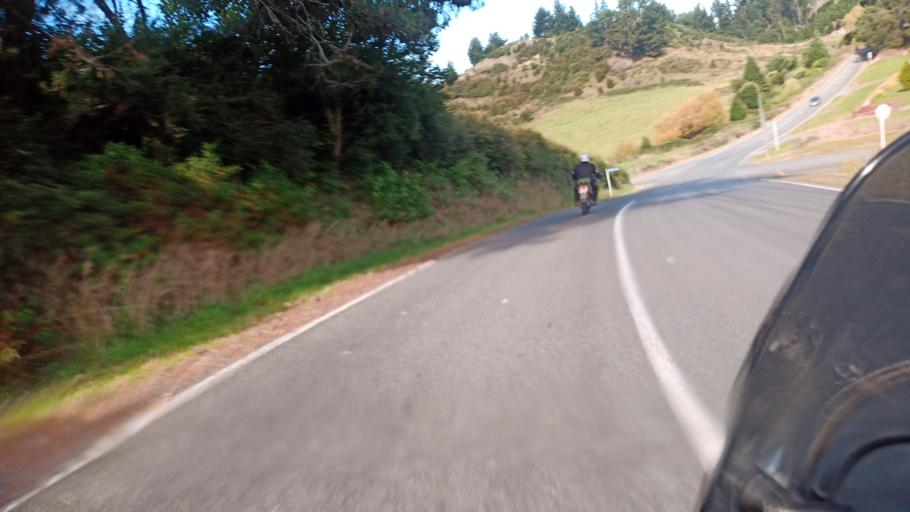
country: NZ
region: Hawke's Bay
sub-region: Wairoa District
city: Wairoa
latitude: -39.0325
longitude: 177.1022
